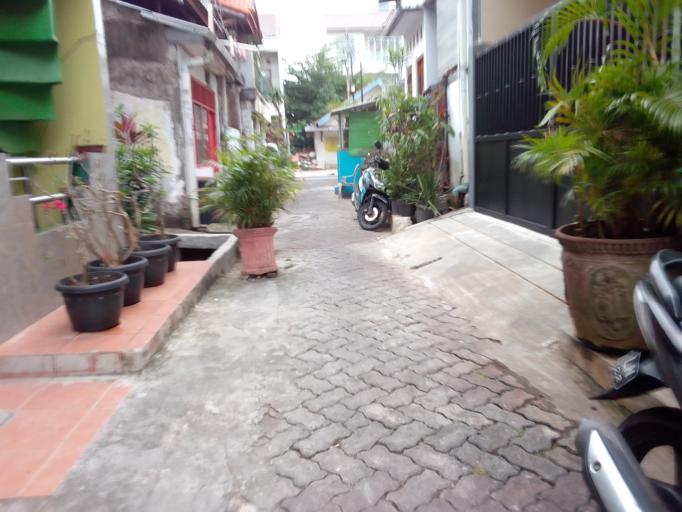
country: ID
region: Jakarta Raya
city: Jakarta
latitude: -6.1719
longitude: 106.8173
